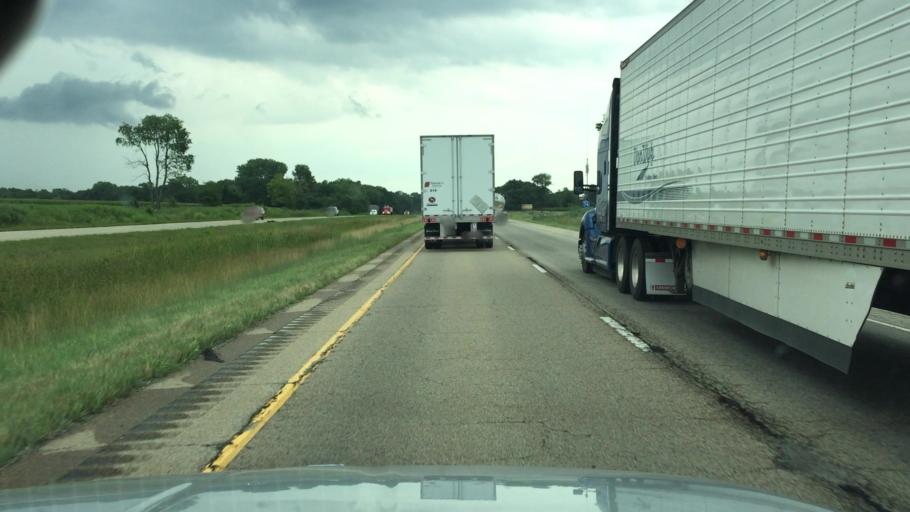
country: US
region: Illinois
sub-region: Peoria County
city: Hanna City
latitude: 40.7716
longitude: -89.7468
